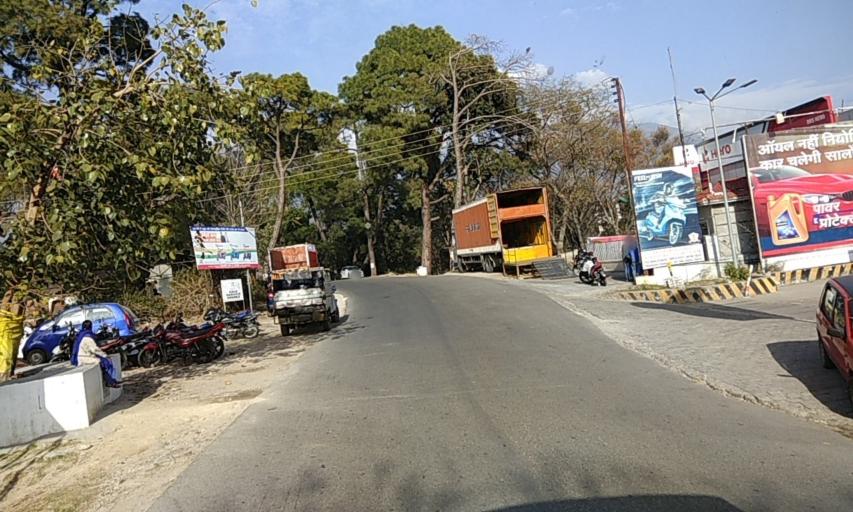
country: IN
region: Himachal Pradesh
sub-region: Kangra
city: Palampur
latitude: 32.0965
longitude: 76.5308
